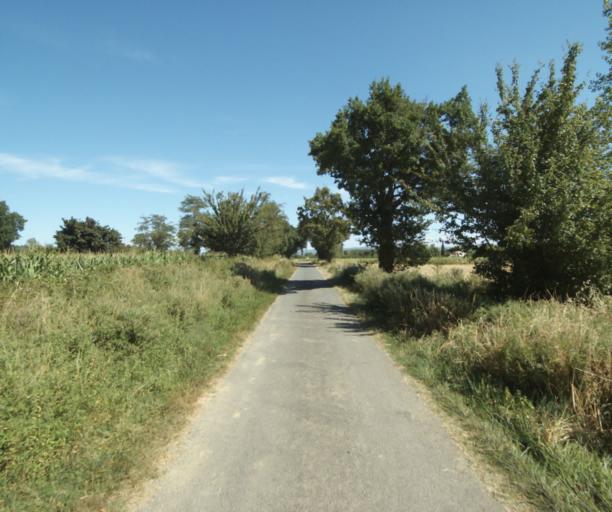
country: FR
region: Midi-Pyrenees
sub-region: Departement de la Haute-Garonne
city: Auriac-sur-Vendinelle
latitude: 43.5195
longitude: 1.8933
